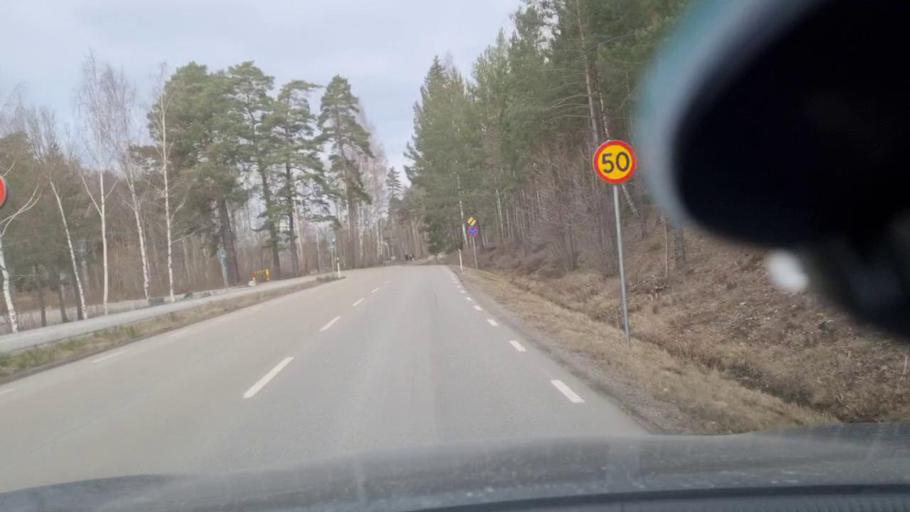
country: SE
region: Stockholm
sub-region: Upplands-Bro Kommun
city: Kungsaengen
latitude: 59.4243
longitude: 17.7730
